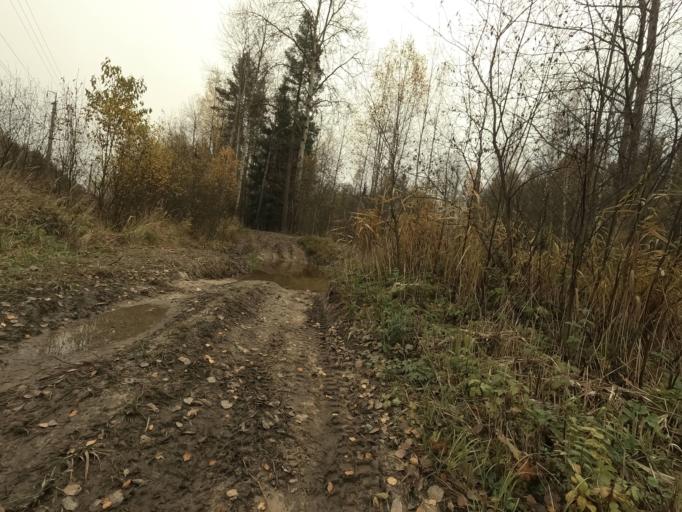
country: RU
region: Leningrad
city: Pavlovo
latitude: 59.7710
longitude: 30.9124
